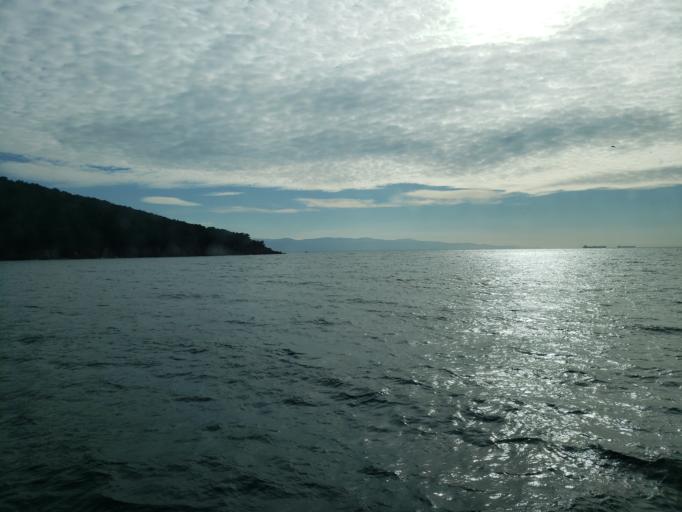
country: TR
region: Istanbul
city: Adalan
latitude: 40.8793
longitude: 29.0758
